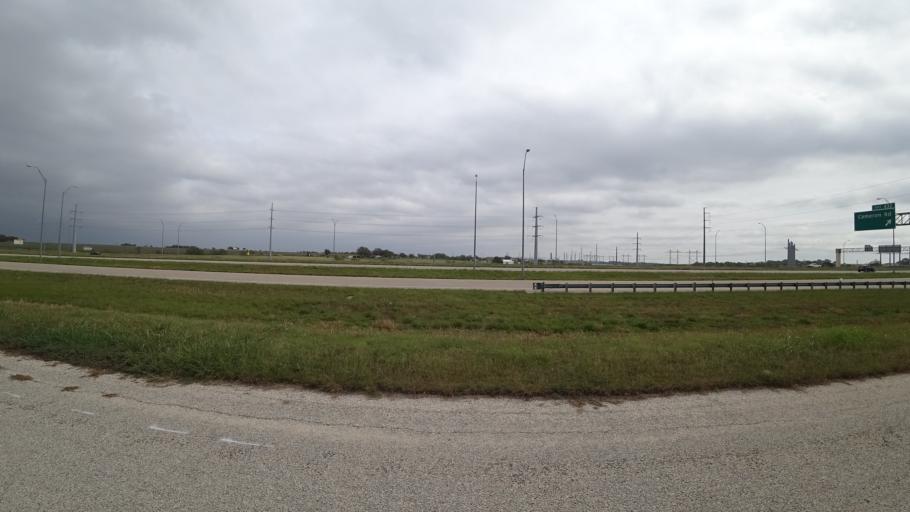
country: US
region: Texas
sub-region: Travis County
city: Pflugerville
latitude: 30.4103
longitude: -97.5855
